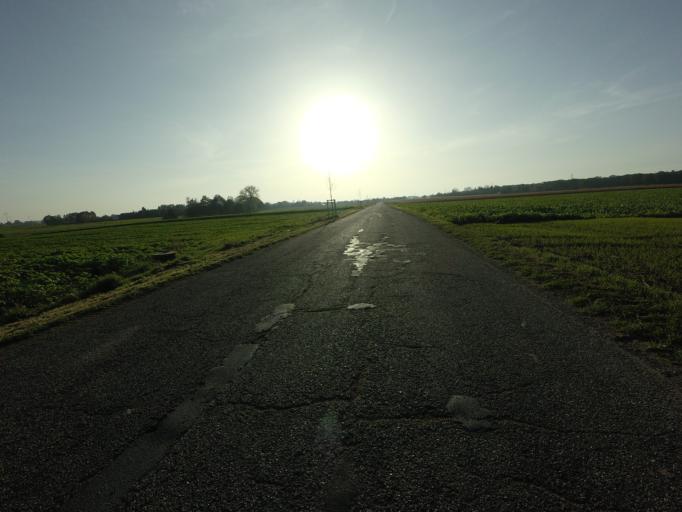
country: DE
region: North Rhine-Westphalia
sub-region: Regierungsbezirk Koln
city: Waldfeucht
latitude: 51.0825
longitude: 6.0001
